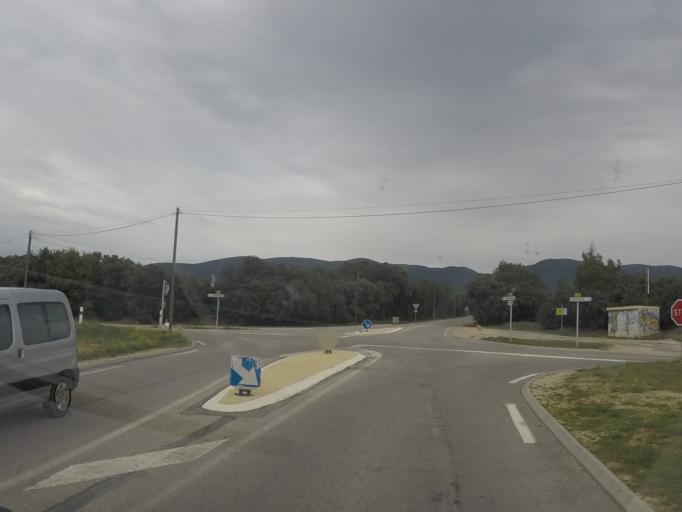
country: FR
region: Provence-Alpes-Cote d'Azur
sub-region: Departement du Vaucluse
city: Cadenet
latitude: 43.7558
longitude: 5.4040
